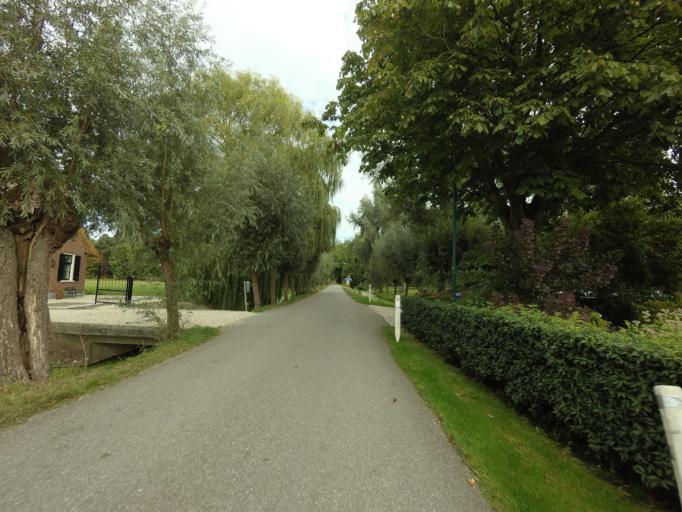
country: NL
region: South Holland
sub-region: Gemeente Schoonhoven
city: Schoonhoven
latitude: 51.9423
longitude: 4.8783
